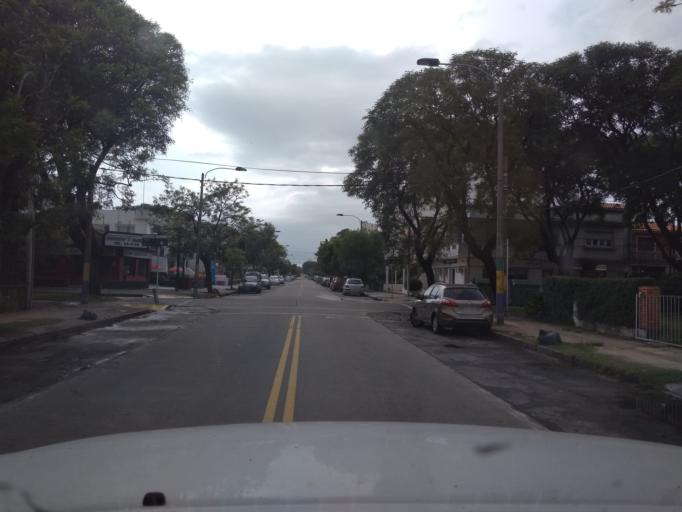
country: UY
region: Canelones
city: Paso de Carrasco
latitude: -34.8958
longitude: -56.1034
